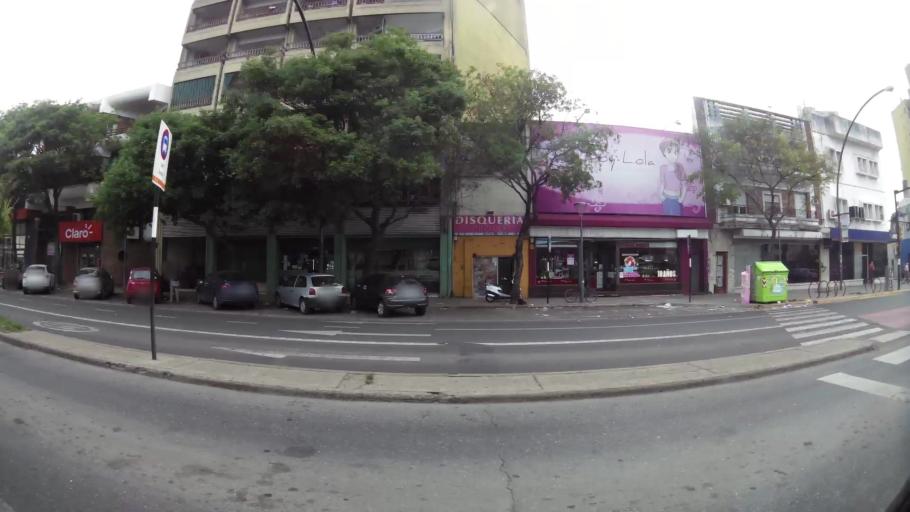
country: AR
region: Santa Fe
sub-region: Departamento de Rosario
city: Rosario
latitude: -32.9204
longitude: -60.6817
